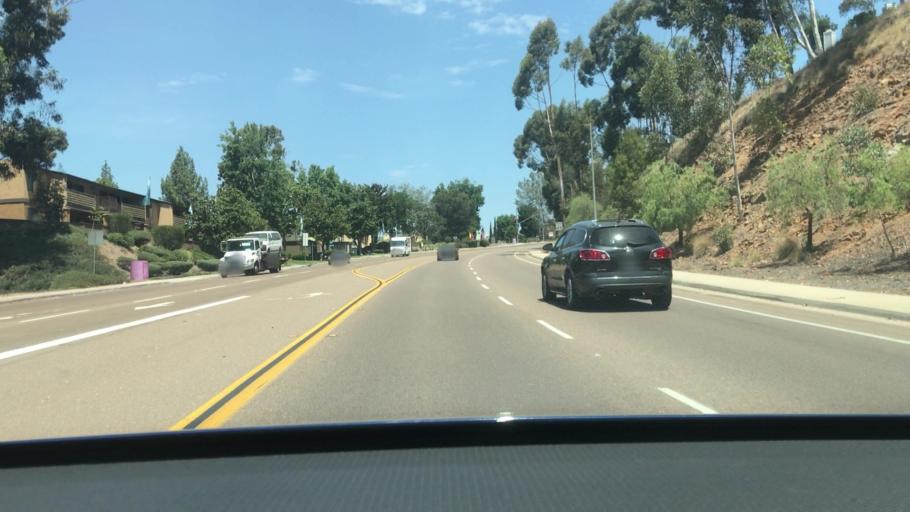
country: US
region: California
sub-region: San Diego County
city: Poway
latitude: 32.9171
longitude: -117.1114
